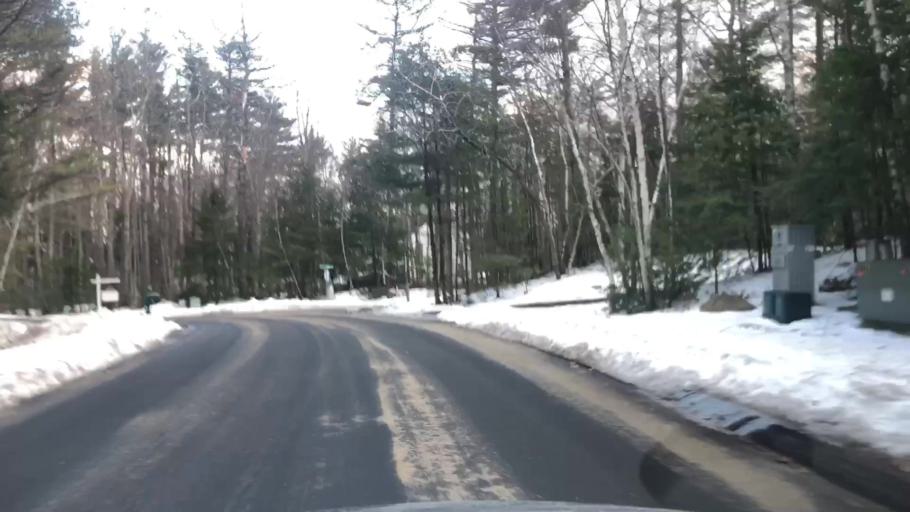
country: US
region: New Hampshire
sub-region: Hillsborough County
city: Milford
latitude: 42.8499
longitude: -71.6227
